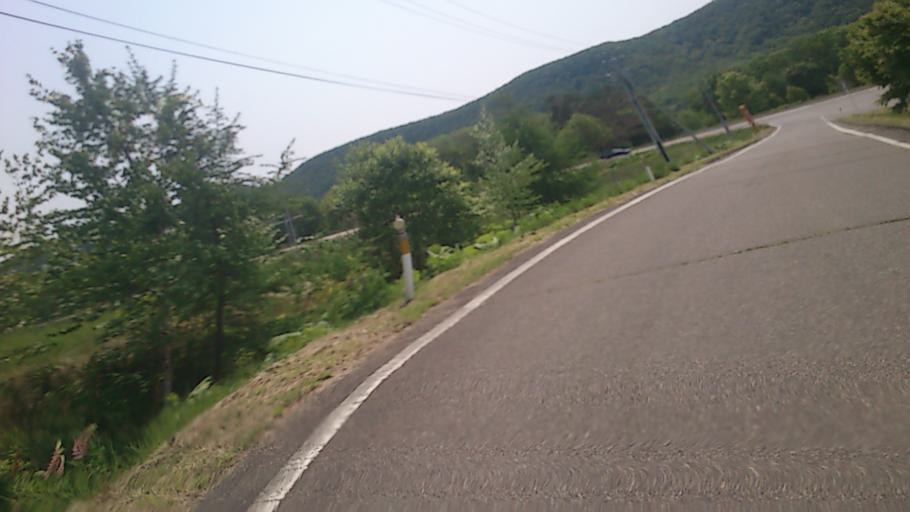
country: JP
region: Hokkaido
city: Otofuke
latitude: 43.2516
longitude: 143.4813
